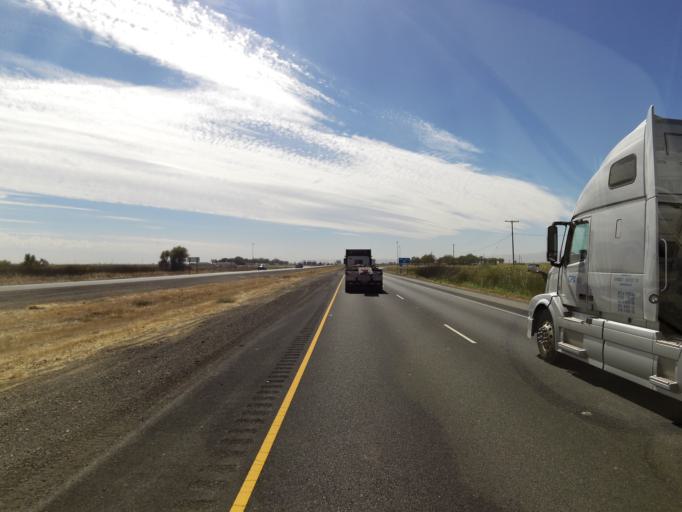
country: US
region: California
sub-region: Colusa County
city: Maxwell
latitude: 39.2467
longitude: -122.1822
